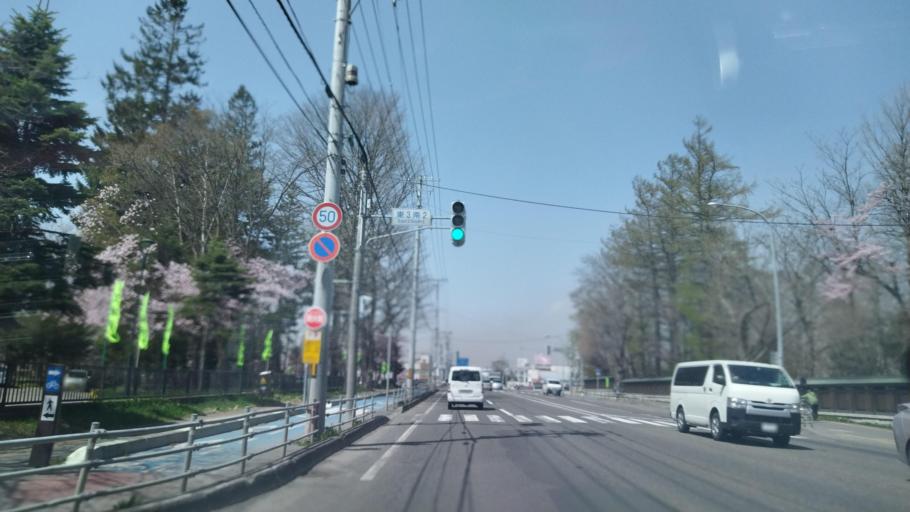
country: JP
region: Hokkaido
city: Obihiro
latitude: 42.9306
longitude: 143.2090
